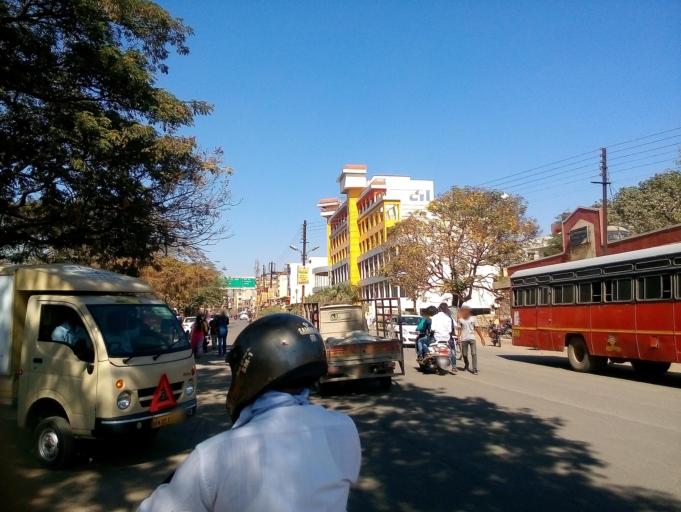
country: IN
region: Maharashtra
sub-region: Aurangabad Division
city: Aurangabad
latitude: 19.8829
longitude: 75.3261
